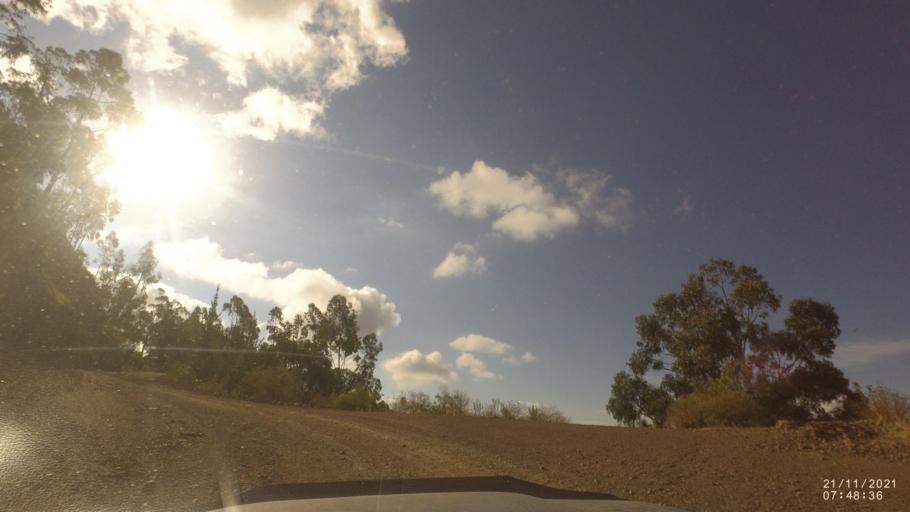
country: BO
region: Cochabamba
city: Cochabamba
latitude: -17.3109
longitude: -66.2173
